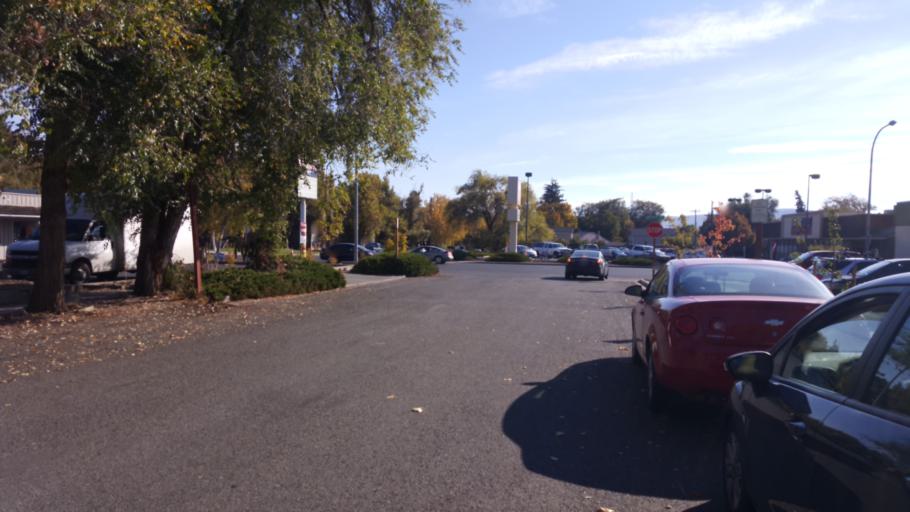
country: US
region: Washington
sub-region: Kittitas County
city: Ellensburg
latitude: 47.0001
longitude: -120.5451
